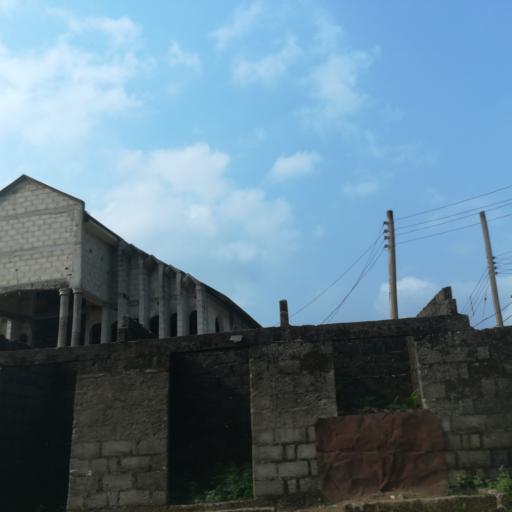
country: NG
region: Rivers
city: Okrika
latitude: 4.7787
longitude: 7.1558
